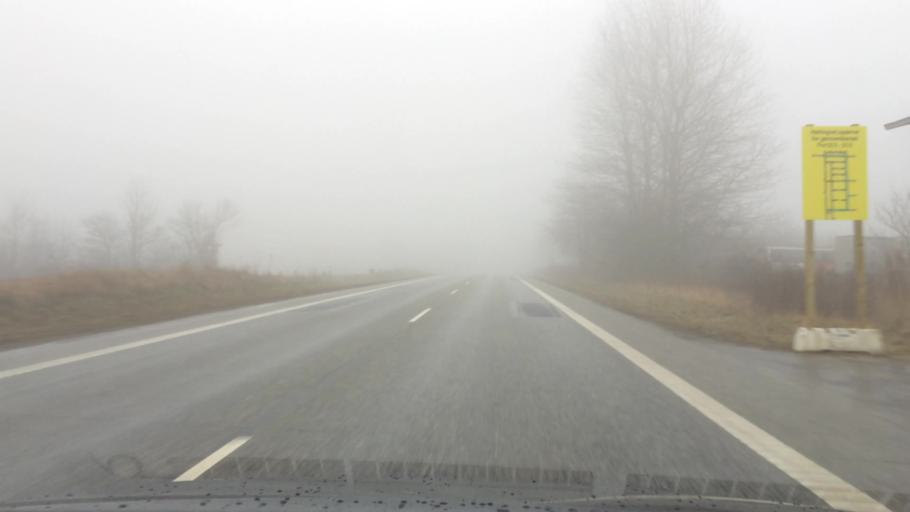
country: DK
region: Central Jutland
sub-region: Horsens Kommune
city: Horsens
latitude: 55.8617
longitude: 9.8021
